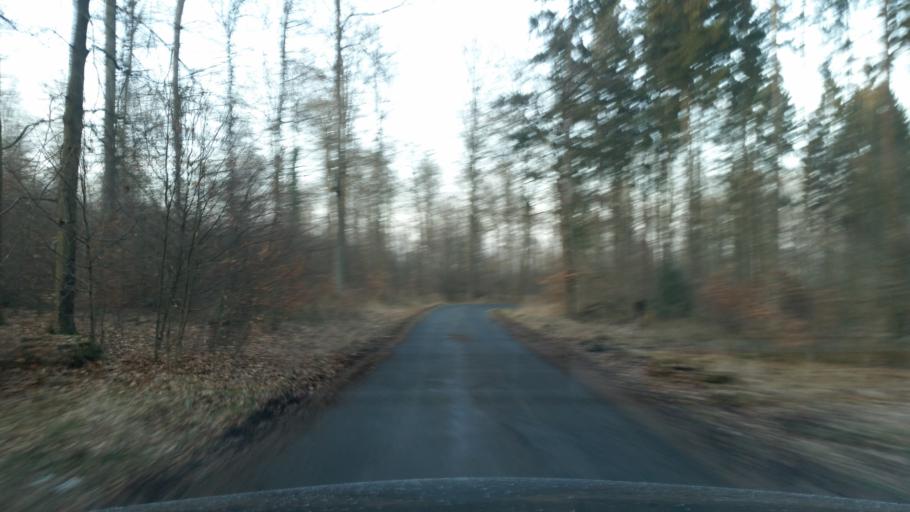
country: DE
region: Lower Saxony
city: Hameln
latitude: 52.0906
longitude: 9.3029
